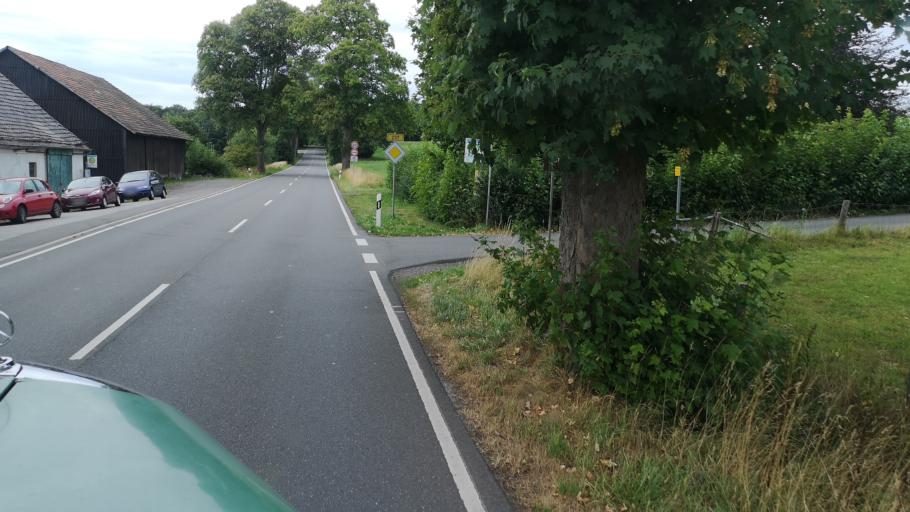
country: DE
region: North Rhine-Westphalia
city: Huckeswagen
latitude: 51.1533
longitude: 7.2910
